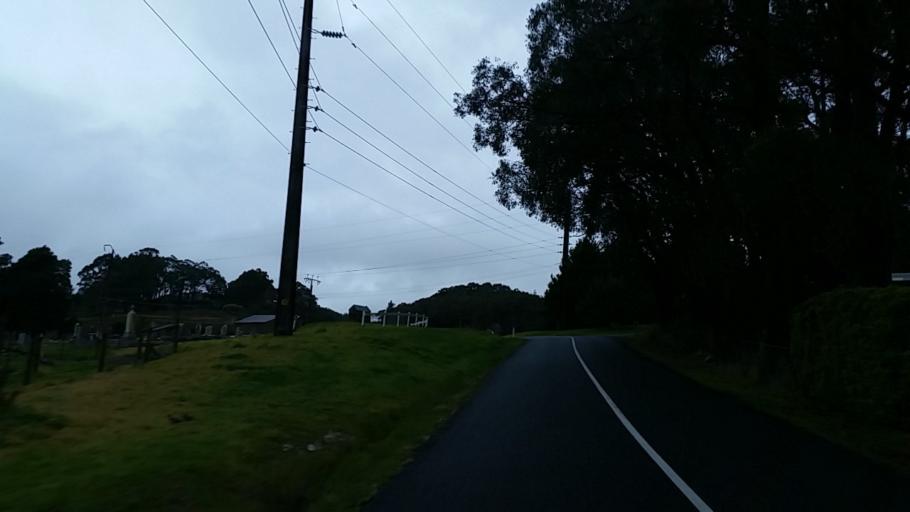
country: AU
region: South Australia
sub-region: Adelaide Hills
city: Bridgewater
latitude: -34.9716
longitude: 138.7383
